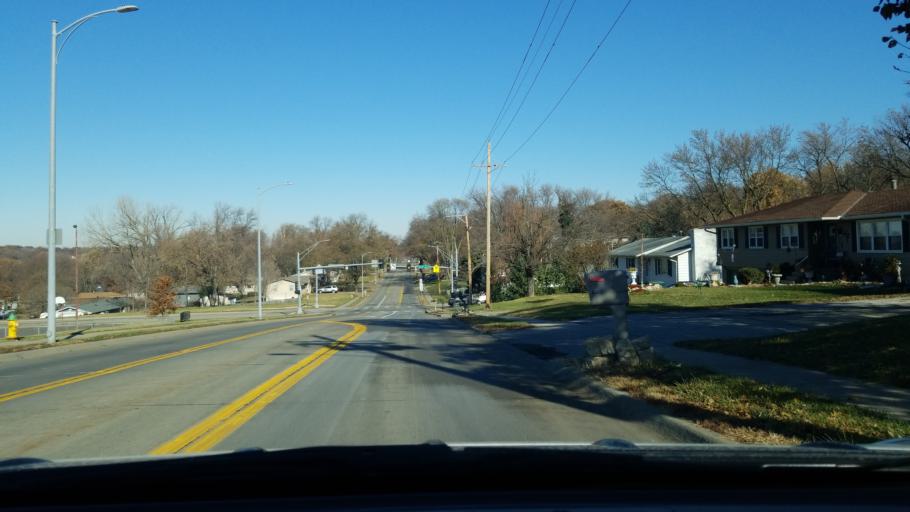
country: US
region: Nebraska
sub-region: Douglas County
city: Ralston
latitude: 41.2256
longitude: -96.0815
